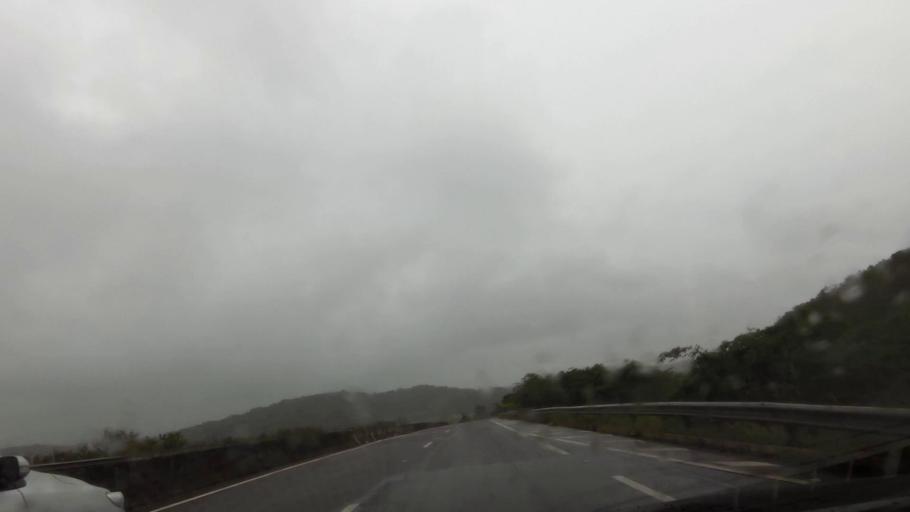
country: BR
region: Espirito Santo
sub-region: Guarapari
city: Guarapari
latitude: -20.6181
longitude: -40.4941
